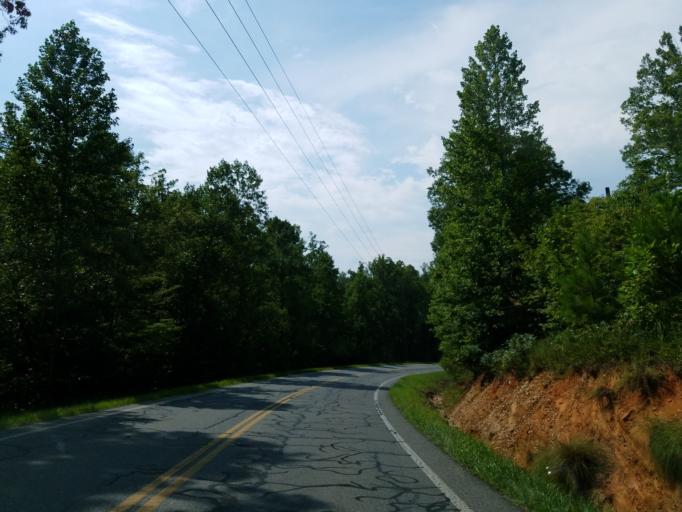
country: US
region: Georgia
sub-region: Gilmer County
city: Ellijay
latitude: 34.5960
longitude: -84.5934
